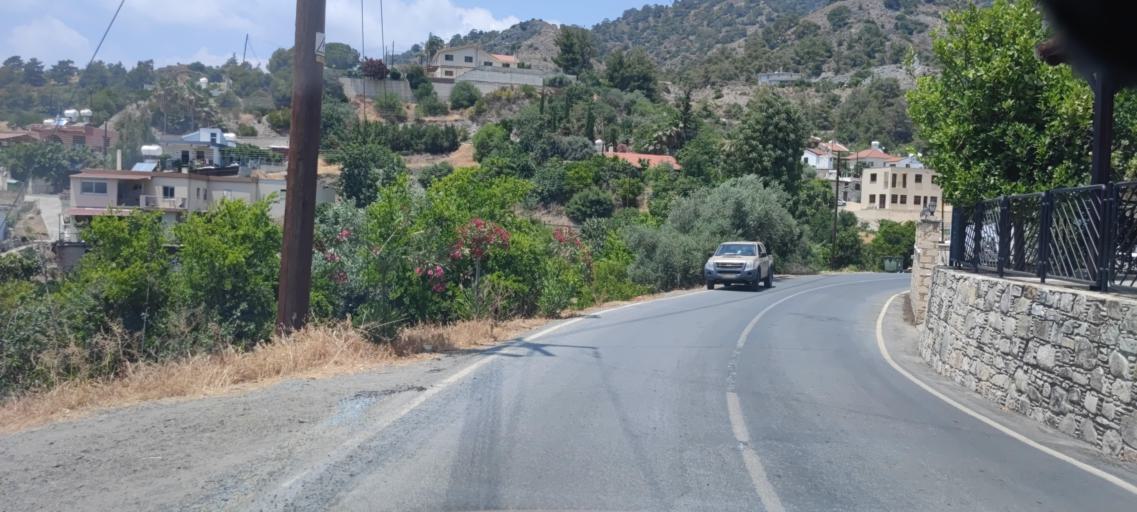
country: CY
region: Limassol
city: Pano Polemidia
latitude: 34.7982
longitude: 33.0215
